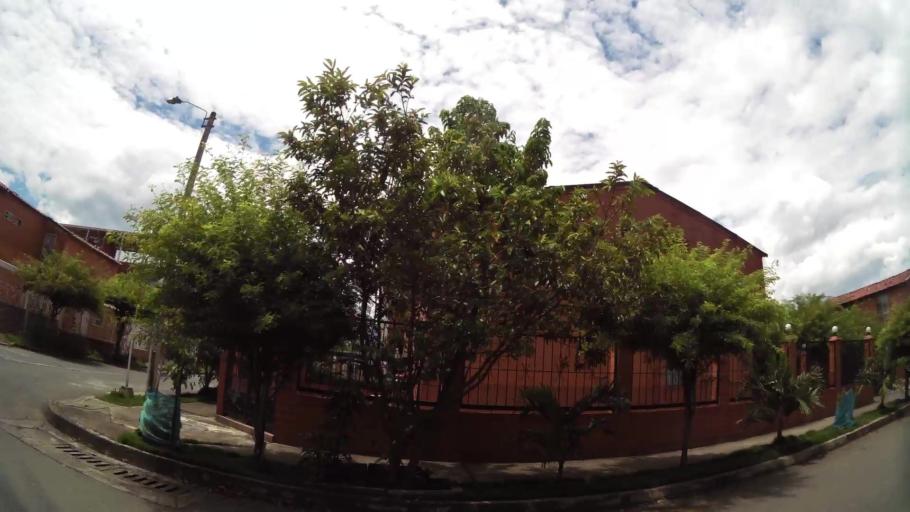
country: CO
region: Valle del Cauca
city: Cali
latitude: 3.3776
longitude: -76.5142
